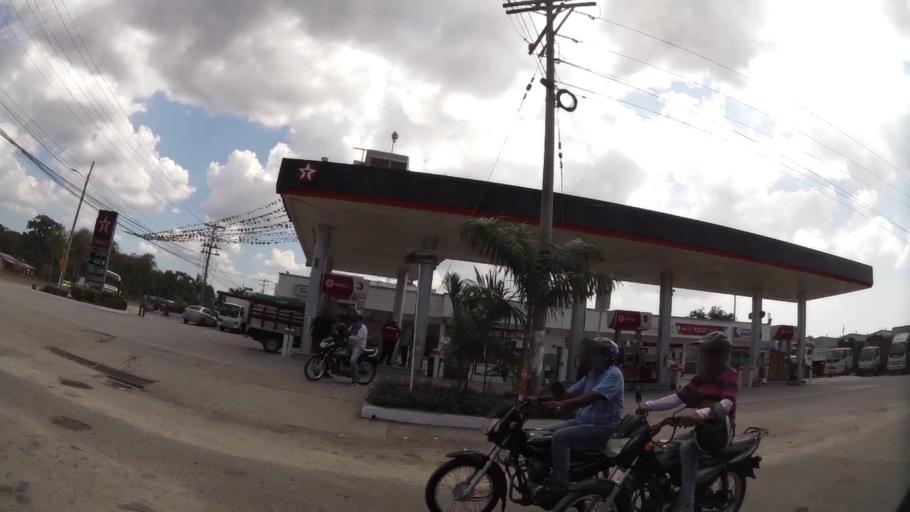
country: CO
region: Bolivar
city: Cartagena
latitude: 10.3759
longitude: -75.4603
